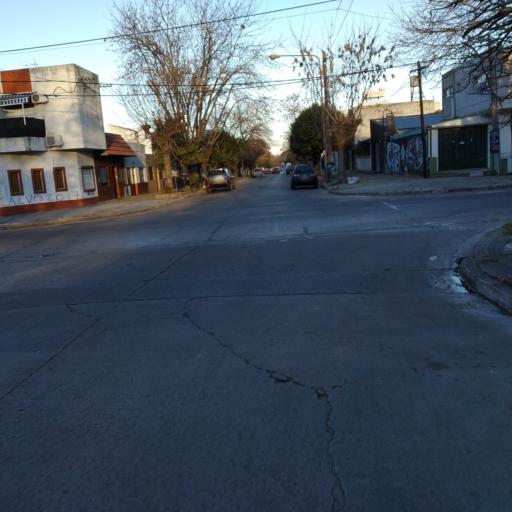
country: AR
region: Buenos Aires
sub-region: Partido de La Plata
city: La Plata
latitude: -34.9456
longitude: -57.9587
